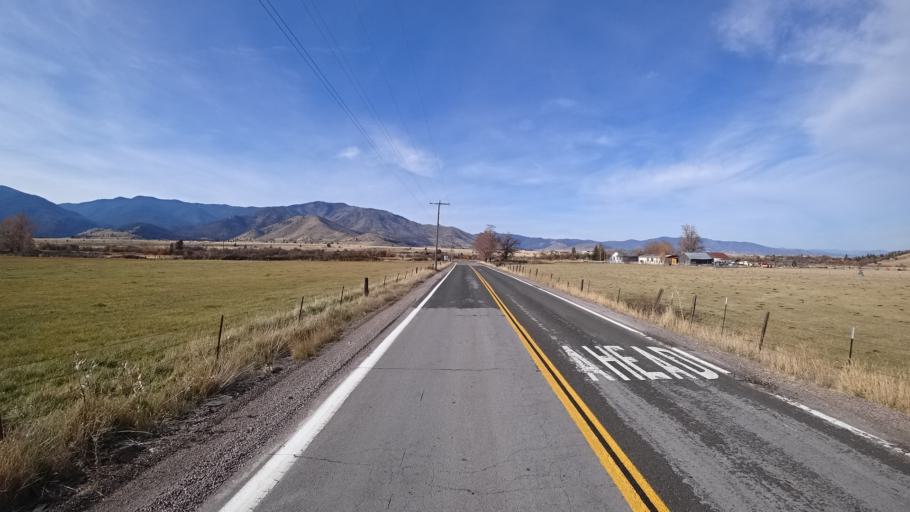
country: US
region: California
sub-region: Siskiyou County
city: Weed
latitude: 41.4678
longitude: -122.4328
